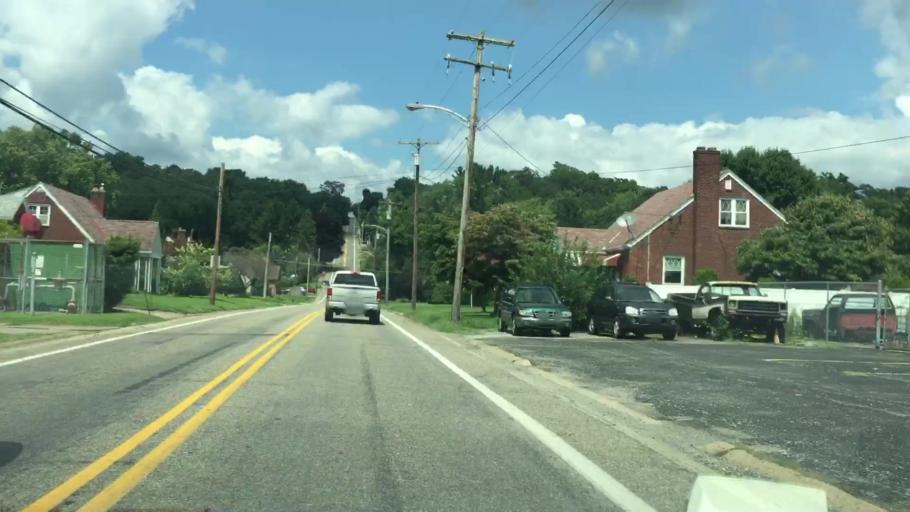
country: US
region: Pennsylvania
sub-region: Allegheny County
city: Cheswick
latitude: 40.5412
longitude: -79.8042
